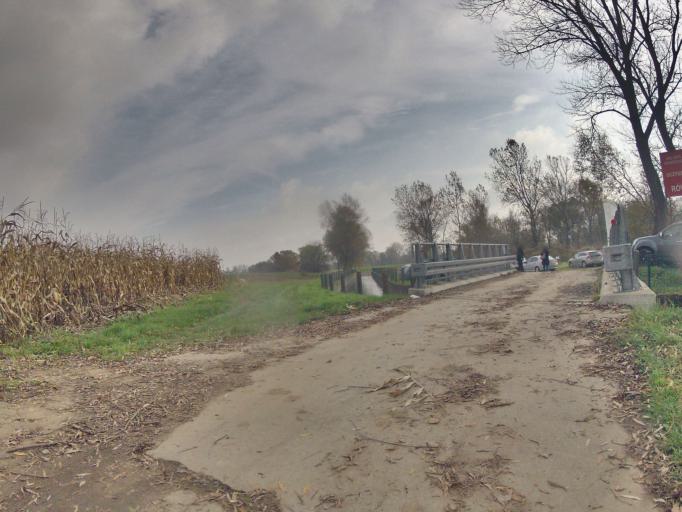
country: PL
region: Lesser Poland Voivodeship
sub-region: Powiat wielicki
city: Wegrzce Wielkie
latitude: 50.0530
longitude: 20.1146
